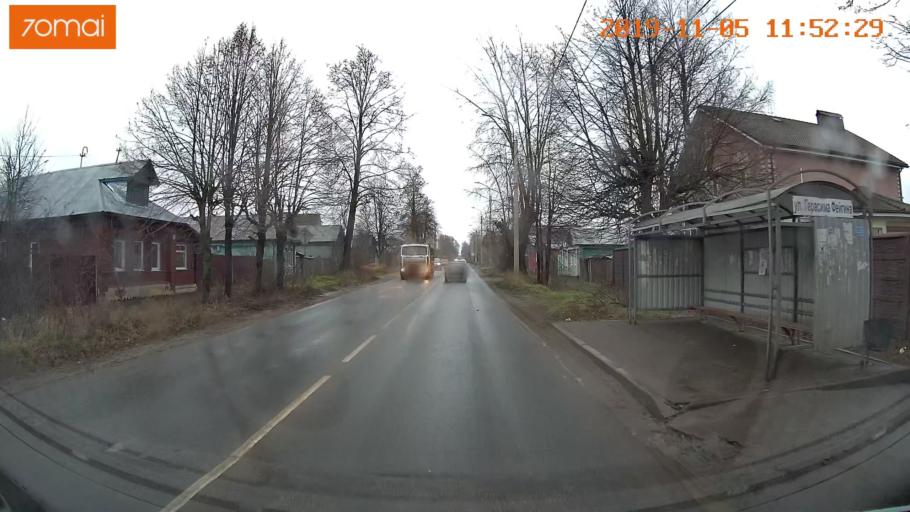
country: RU
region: Ivanovo
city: Bogorodskoye
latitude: 57.0001
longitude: 41.0294
